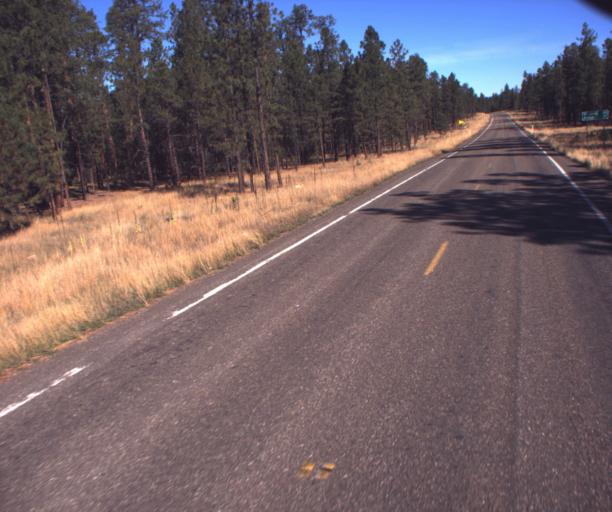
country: US
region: Arizona
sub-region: Coconino County
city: Fredonia
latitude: 36.7275
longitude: -112.2125
